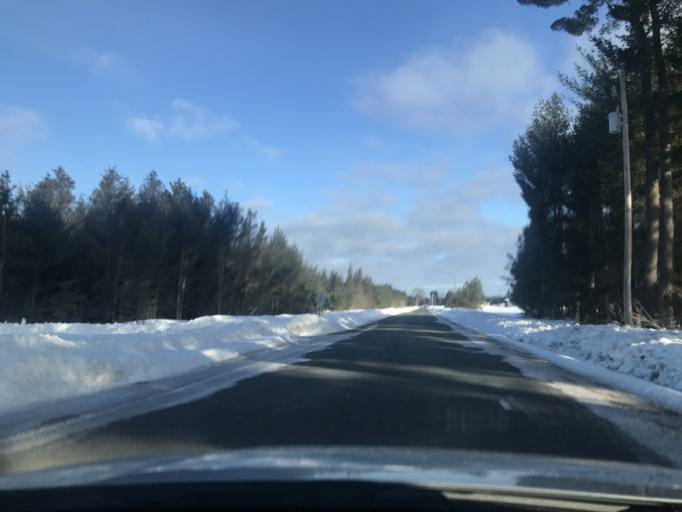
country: US
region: Wisconsin
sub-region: Marinette County
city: Niagara
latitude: 45.6114
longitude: -87.9769
